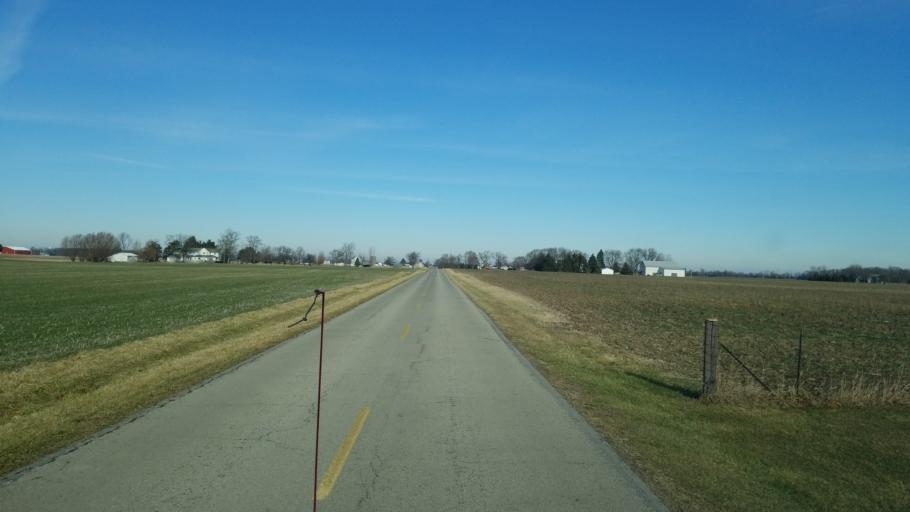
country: US
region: Ohio
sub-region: Putnam County
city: Pandora
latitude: 40.9145
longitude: -83.9377
